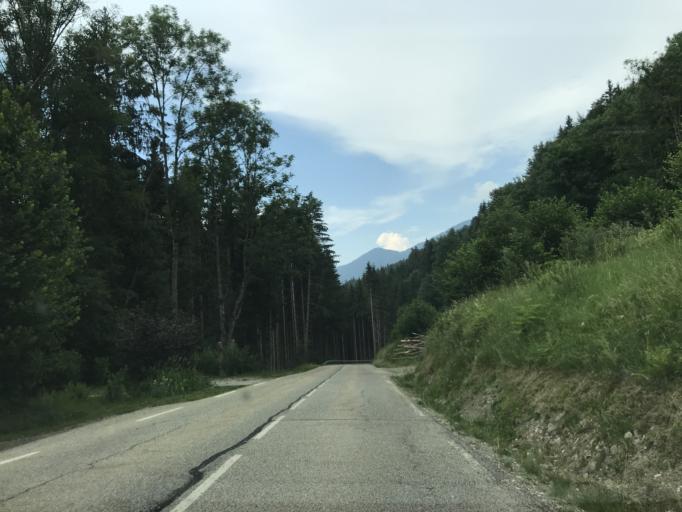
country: FR
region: Rhone-Alpes
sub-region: Departement de l'Isere
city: Allevard
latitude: 45.3267
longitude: 6.0904
